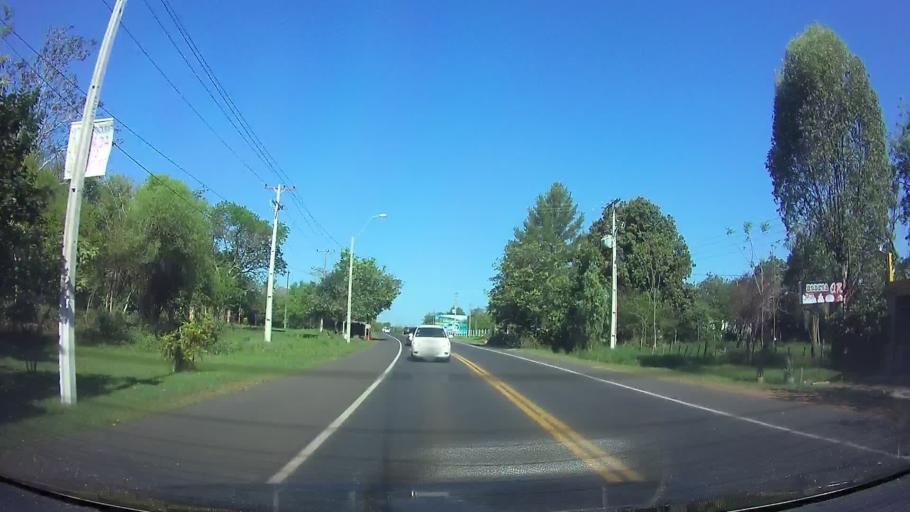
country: PY
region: Central
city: Itaugua
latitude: -25.3404
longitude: -57.3482
